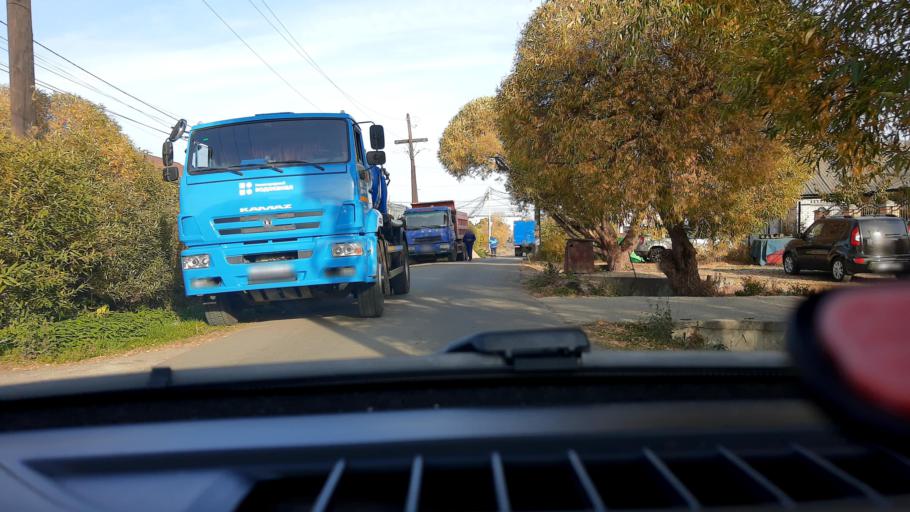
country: RU
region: Nizjnij Novgorod
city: Nizhniy Novgorod
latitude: 56.2883
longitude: 43.8950
